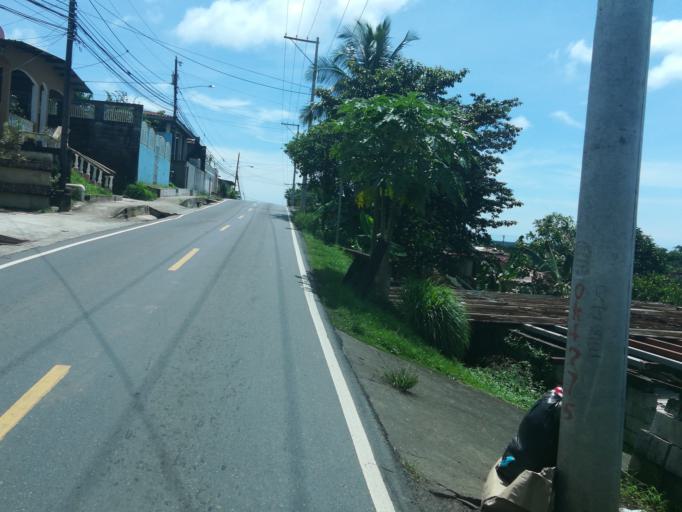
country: PA
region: Panama
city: Tocumen
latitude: 9.0937
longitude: -79.4041
